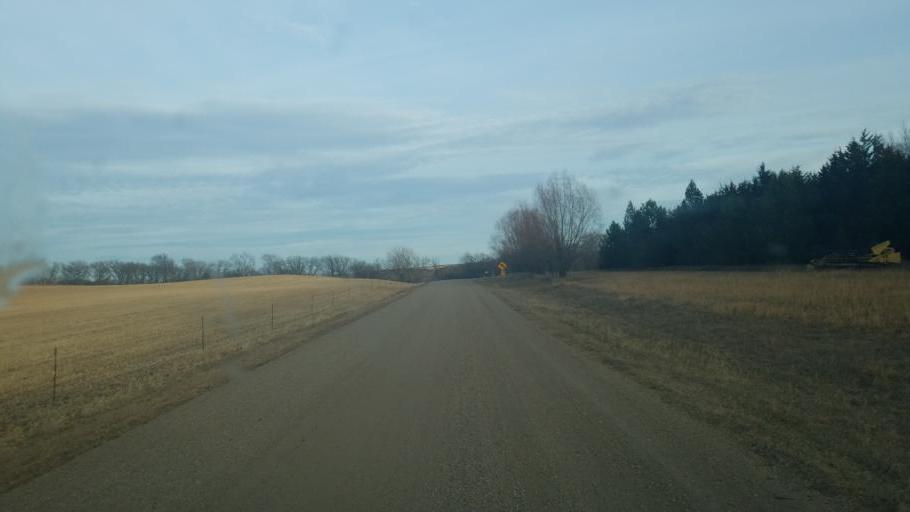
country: US
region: Nebraska
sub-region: Knox County
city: Center
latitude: 42.6851
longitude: -97.8154
